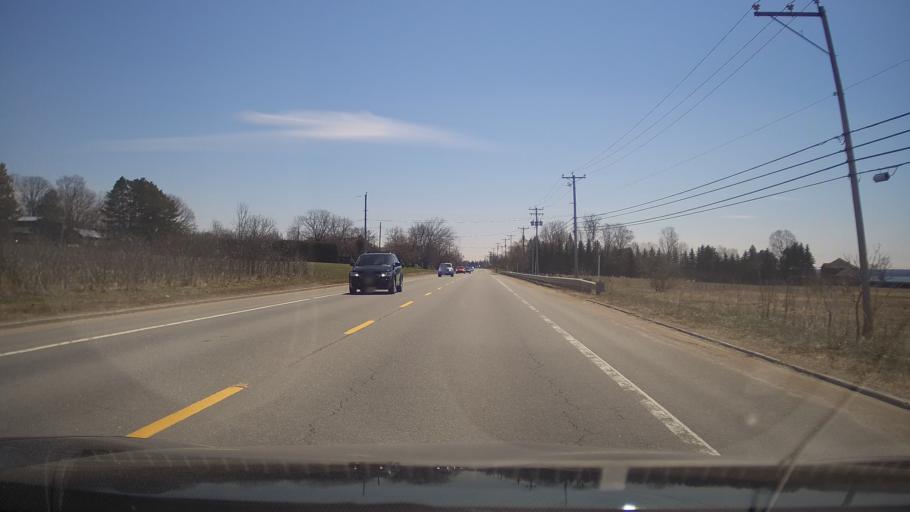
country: CA
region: Ontario
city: Bells Corners
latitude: 45.4256
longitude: -75.8949
